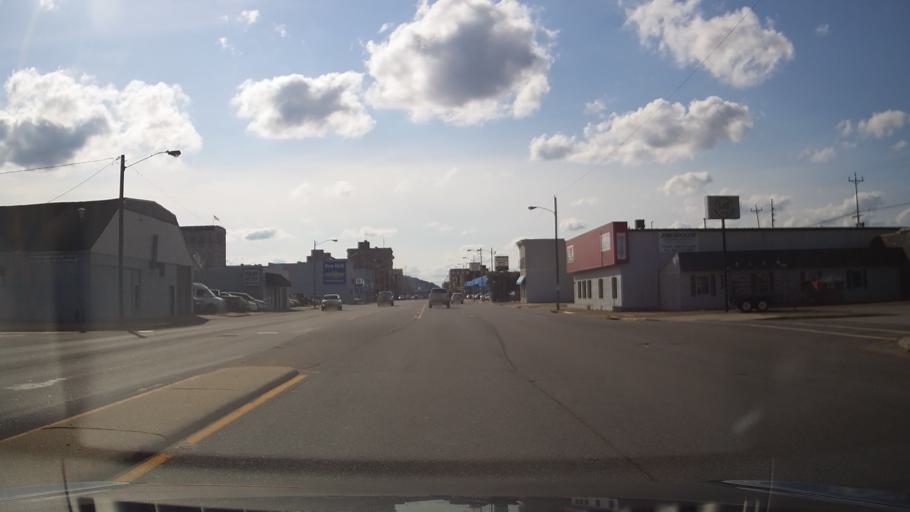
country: US
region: Kentucky
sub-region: Boyd County
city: Ashland
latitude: 38.4772
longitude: -82.6340
